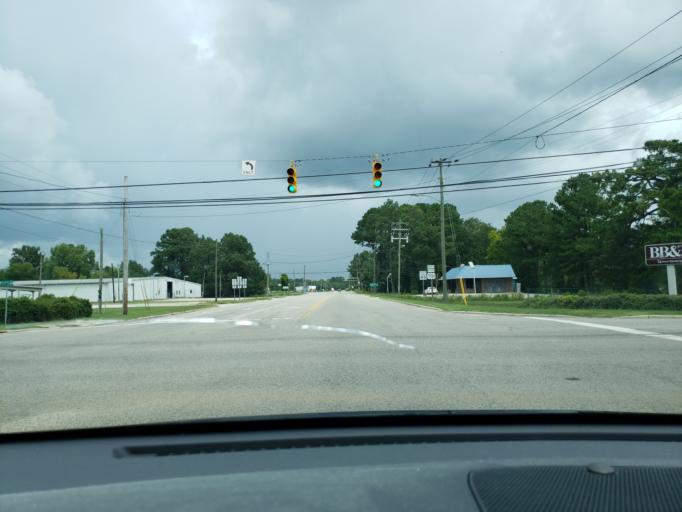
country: US
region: North Carolina
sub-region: Bladen County
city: Bladenboro
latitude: 34.4897
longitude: -78.6618
